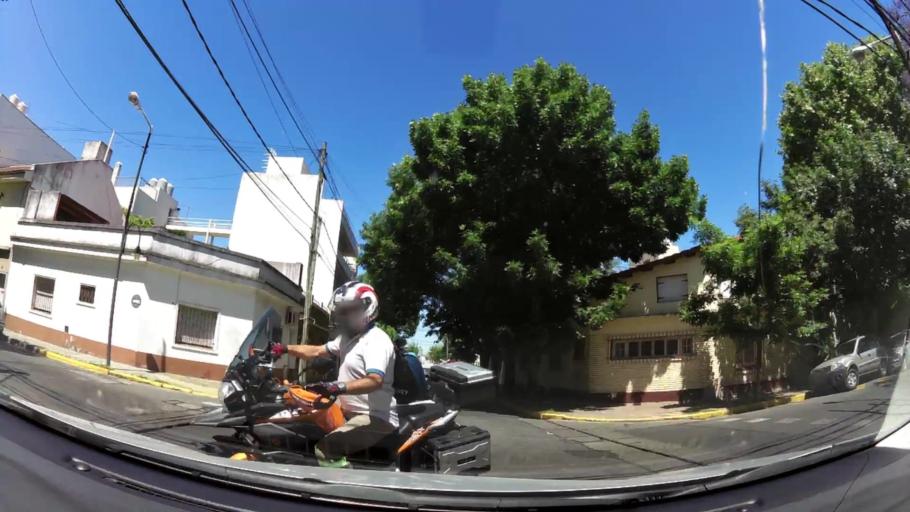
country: AR
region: Buenos Aires
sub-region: Partido de San Isidro
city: San Isidro
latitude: -34.4559
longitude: -58.5391
